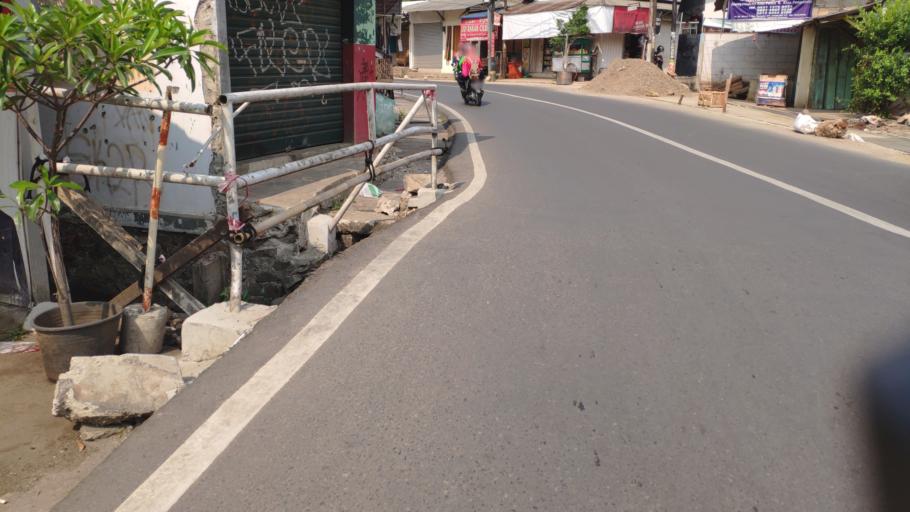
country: ID
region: West Java
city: Pamulang
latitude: -6.3178
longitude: 106.8114
